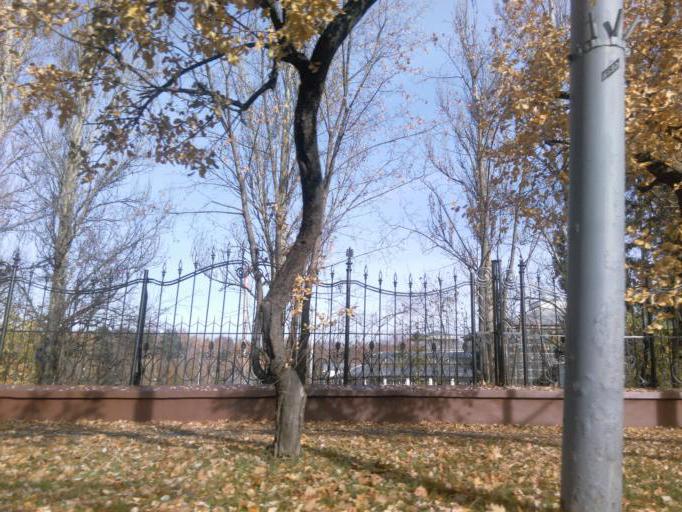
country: RU
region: Moscow
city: Novovladykino
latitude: 55.8335
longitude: 37.5953
